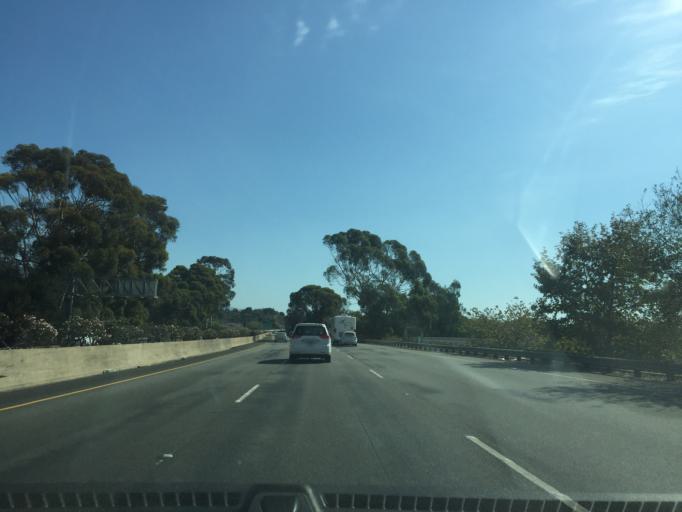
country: US
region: California
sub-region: Santa Barbara County
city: Goleta
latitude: 34.4420
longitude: -119.7850
